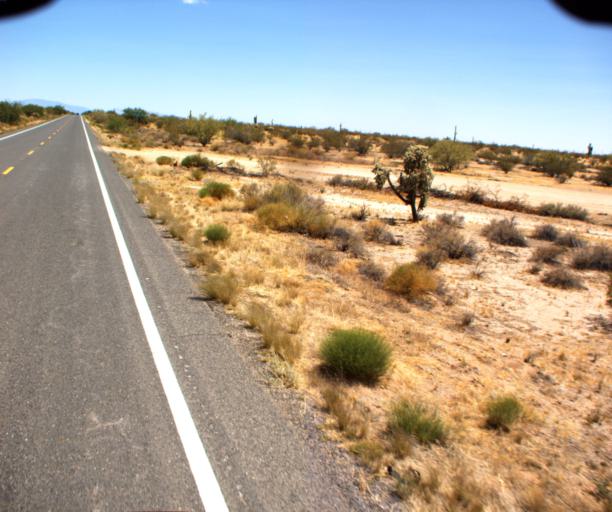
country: US
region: Arizona
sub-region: Pinal County
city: Florence
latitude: 32.8745
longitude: -111.2537
